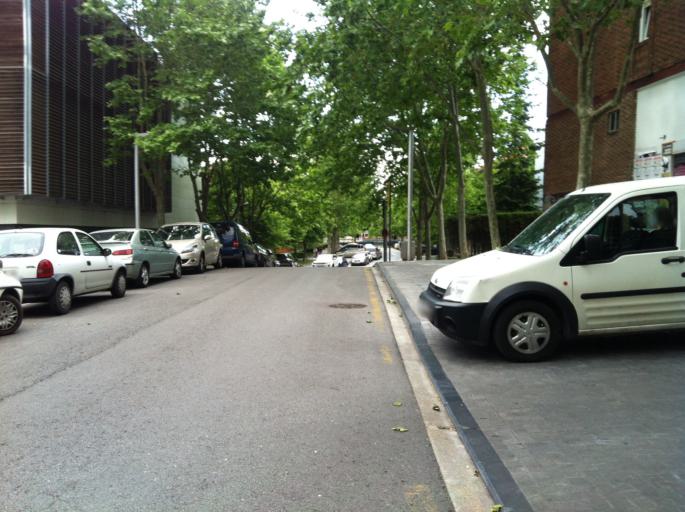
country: ES
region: Basque Country
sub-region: Provincia de Alava
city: Gasteiz / Vitoria
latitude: 42.8388
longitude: -2.6706
